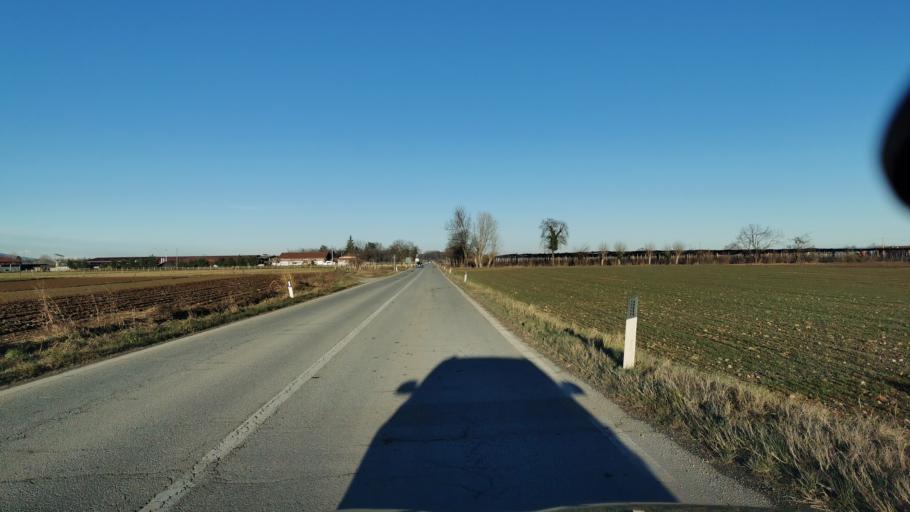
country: IT
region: Piedmont
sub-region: Provincia di Cuneo
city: Caraglio
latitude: 44.4328
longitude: 7.4421
